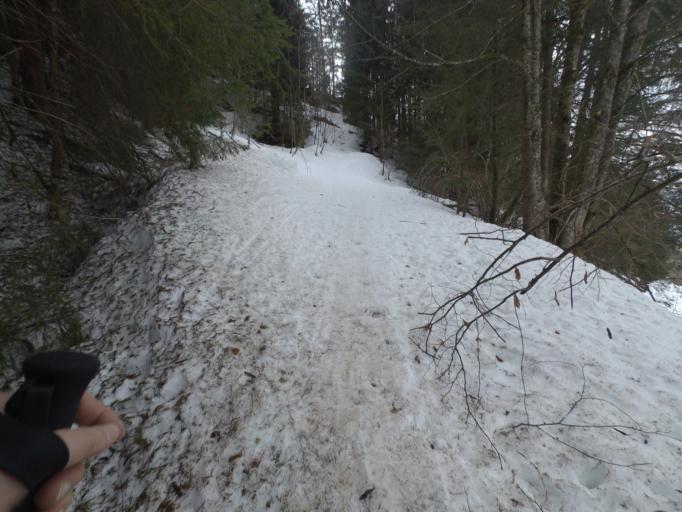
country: AT
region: Salzburg
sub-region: Politischer Bezirk Sankt Johann im Pongau
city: Sankt Johann im Pongau
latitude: 47.3293
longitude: 13.2109
